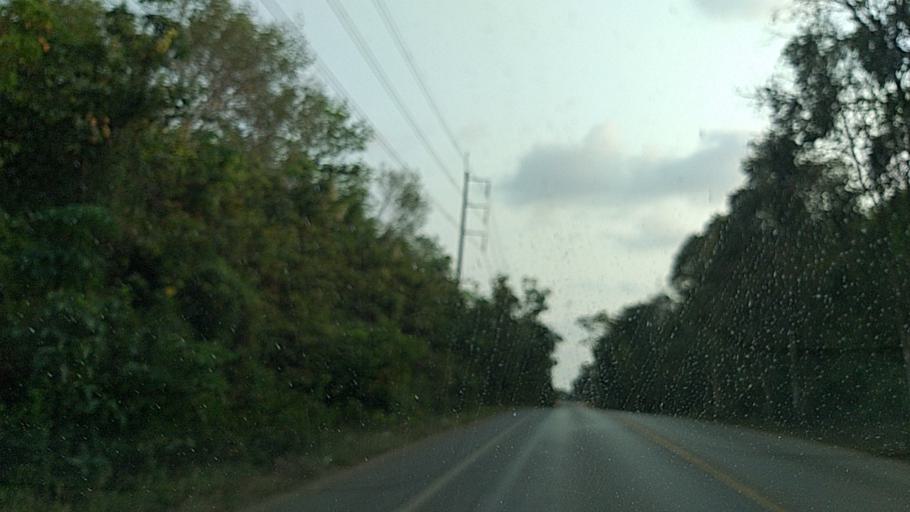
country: TH
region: Trat
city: Khao Saming
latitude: 12.3589
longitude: 102.3831
